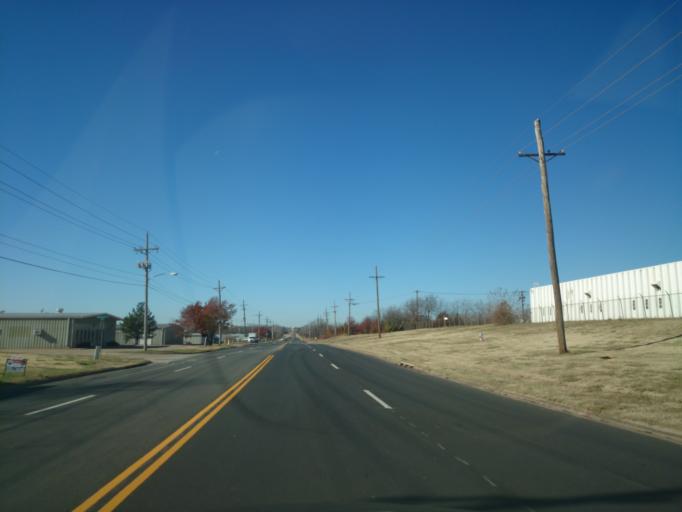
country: US
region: Oklahoma
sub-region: Payne County
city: Stillwater
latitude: 36.1595
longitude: -97.0534
